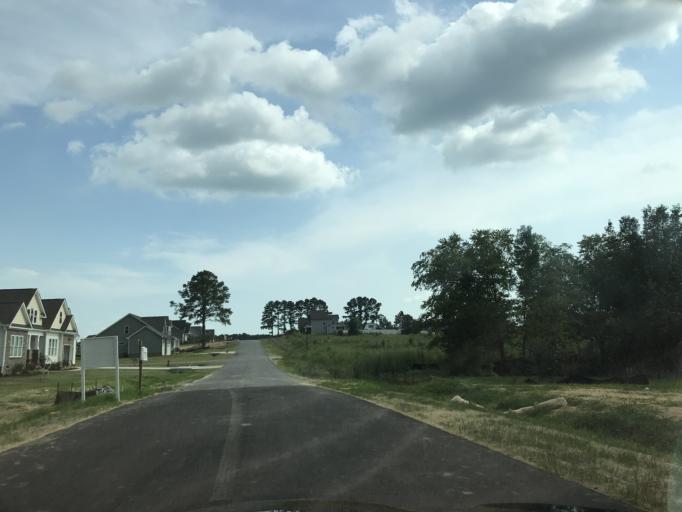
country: US
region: North Carolina
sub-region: Johnston County
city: Four Oaks
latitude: 35.5193
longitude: -78.5314
